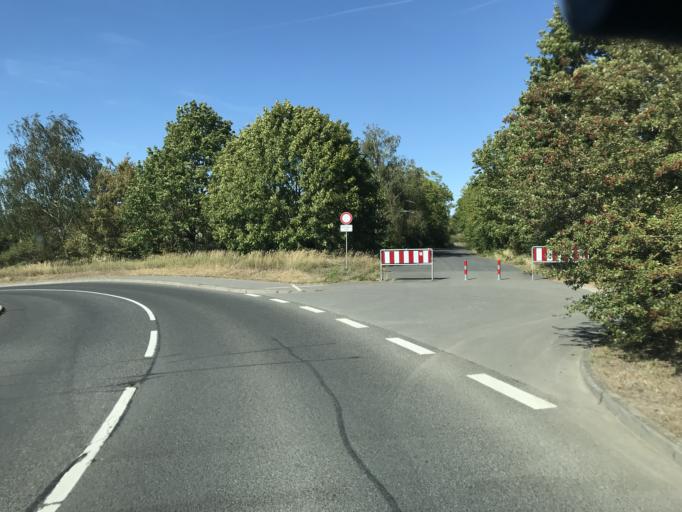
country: DE
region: Hesse
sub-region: Regierungsbezirk Darmstadt
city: Hochheim am Main
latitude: 50.0489
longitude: 8.3019
